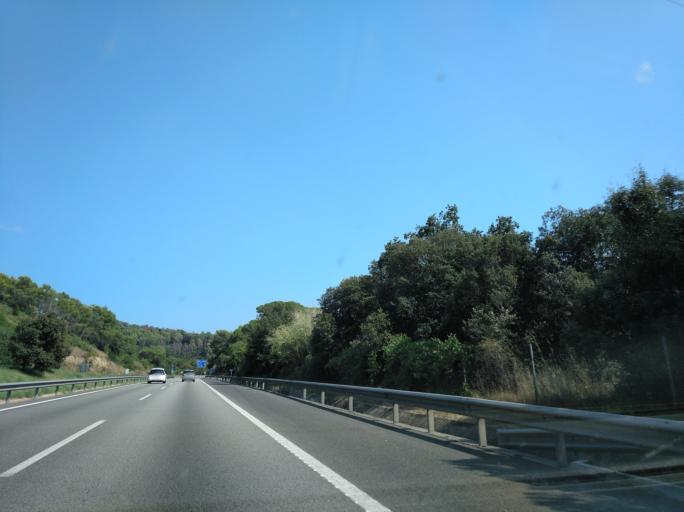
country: ES
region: Catalonia
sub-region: Provincia de Barcelona
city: Argentona
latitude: 41.5799
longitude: 2.3767
